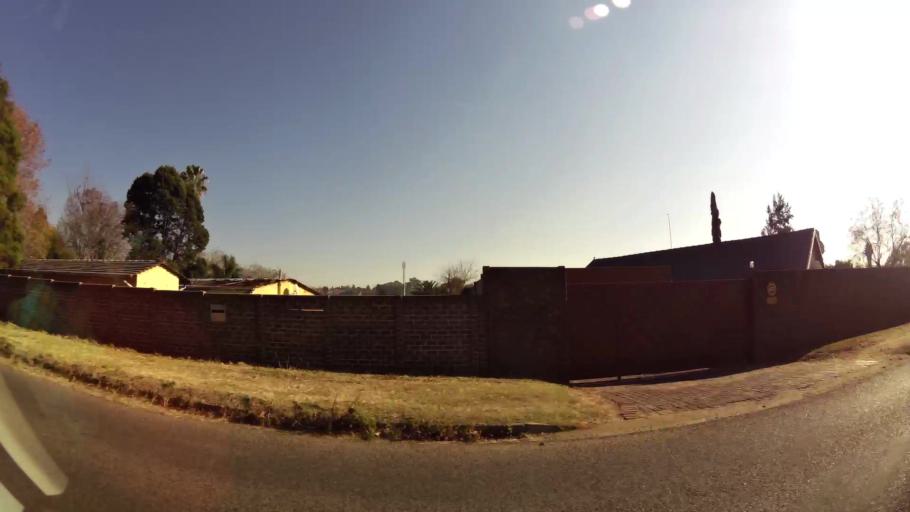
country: ZA
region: Gauteng
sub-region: City of Johannesburg Metropolitan Municipality
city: Modderfontein
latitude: -26.1338
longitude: 28.1448
